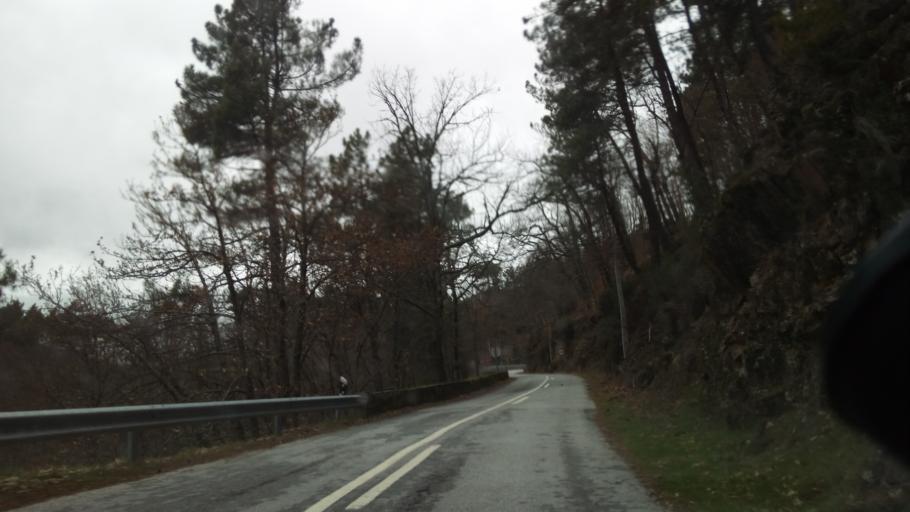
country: PT
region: Guarda
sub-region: Manteigas
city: Manteigas
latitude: 40.4116
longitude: -7.5295
